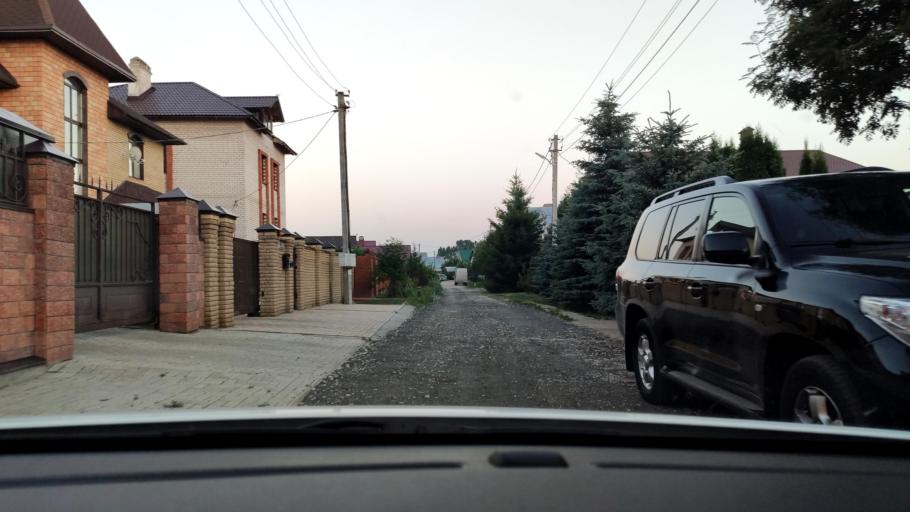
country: RU
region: Tatarstan
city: Stolbishchi
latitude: 55.7732
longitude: 49.2698
